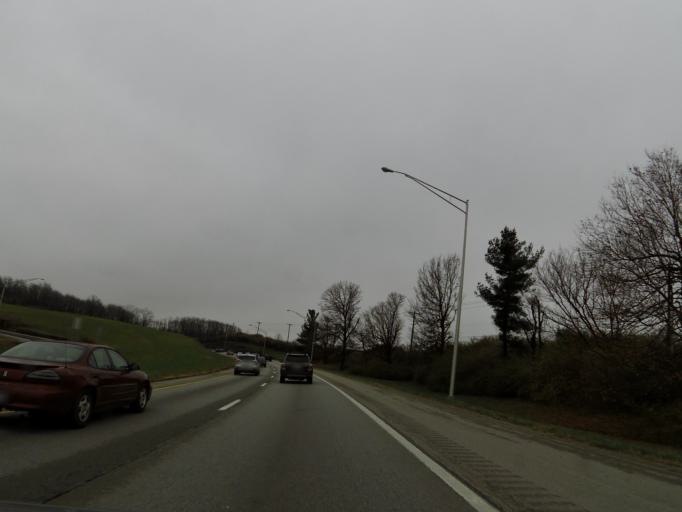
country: US
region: Kentucky
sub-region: Fayette County
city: Lexington-Fayette
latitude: 38.1126
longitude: -84.5234
